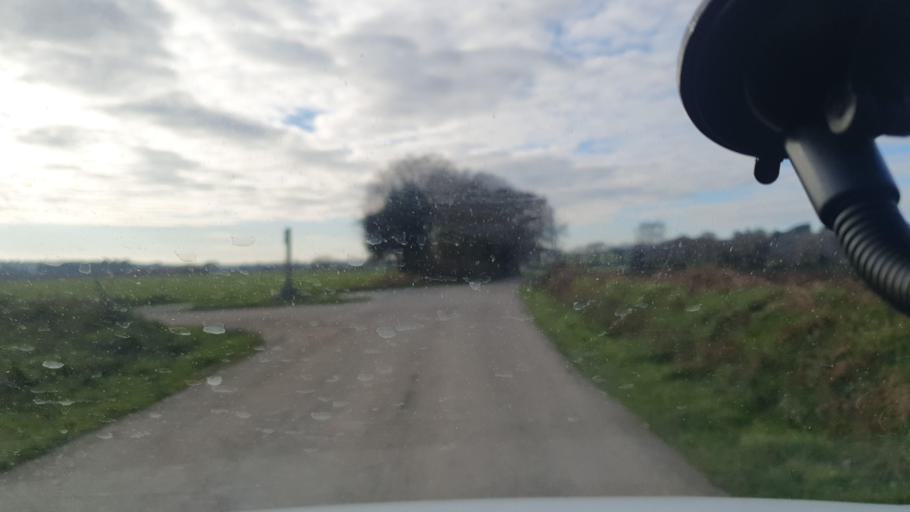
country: FR
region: Brittany
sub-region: Departement du Finistere
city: Landrevarzec
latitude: 48.1062
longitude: -4.0422
